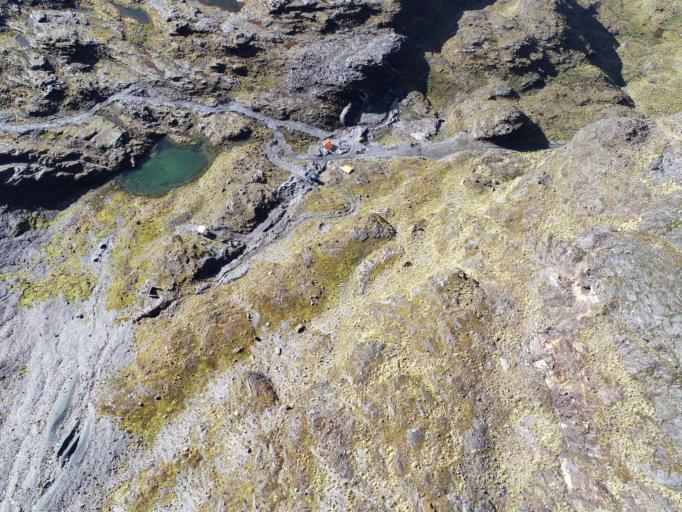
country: PE
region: Puno
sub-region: San Antonio De Putina
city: Sina
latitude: -14.7394
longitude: -69.0536
